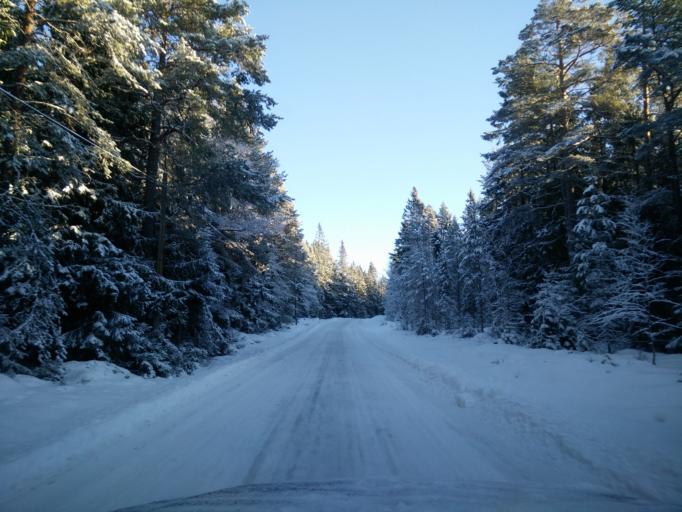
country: SE
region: Vaesternorrland
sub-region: Sundsvalls Kommun
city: Njurundabommen
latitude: 62.2357
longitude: 17.6112
